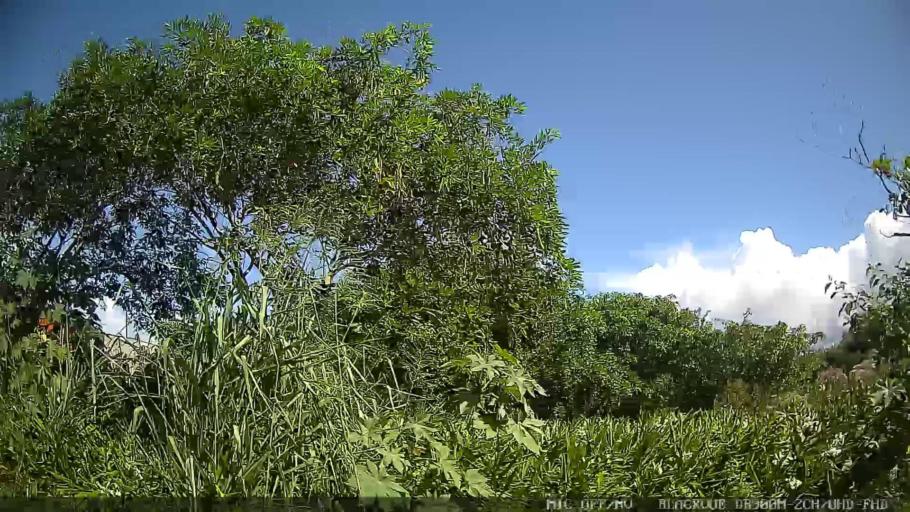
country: BR
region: Sao Paulo
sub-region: Itanhaem
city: Itanhaem
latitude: -24.2305
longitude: -46.8756
